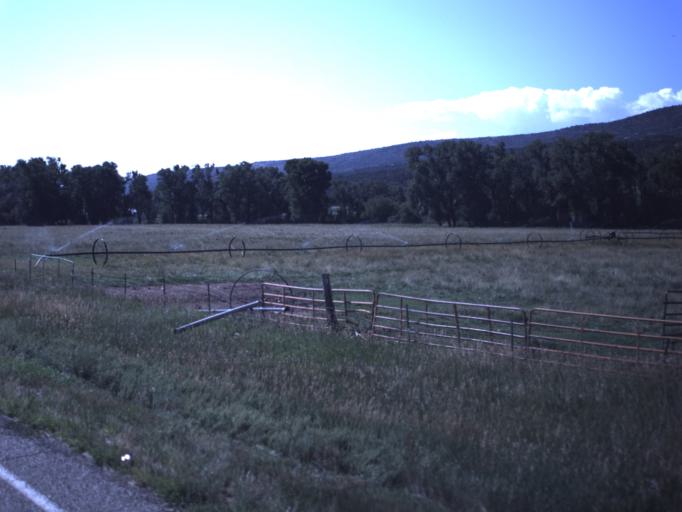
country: US
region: Utah
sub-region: Duchesne County
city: Duchesne
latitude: 40.3768
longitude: -110.7333
